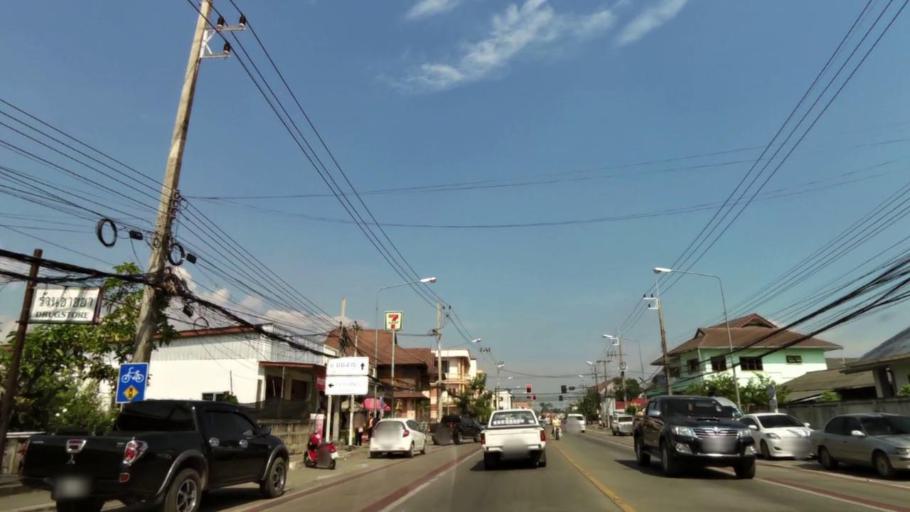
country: TH
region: Chiang Rai
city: Chiang Rai
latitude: 19.9253
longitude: 99.8359
